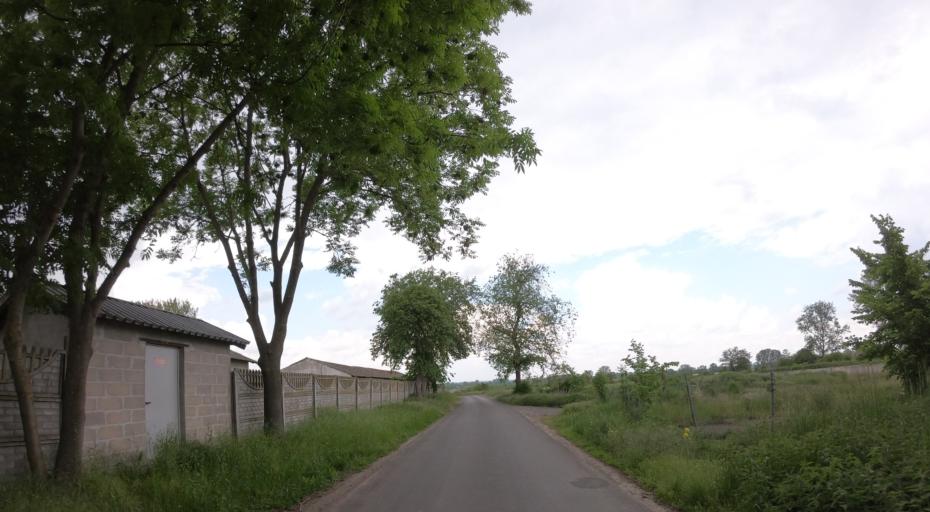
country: PL
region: West Pomeranian Voivodeship
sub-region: Powiat pyrzycki
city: Bielice
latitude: 53.2042
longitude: 14.7692
